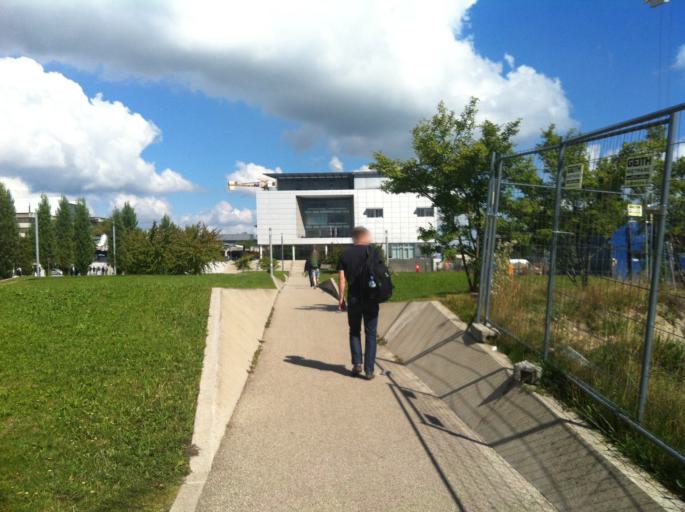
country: DE
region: Bavaria
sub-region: Upper Bavaria
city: Garching bei Munchen
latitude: 48.2656
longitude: 11.6718
